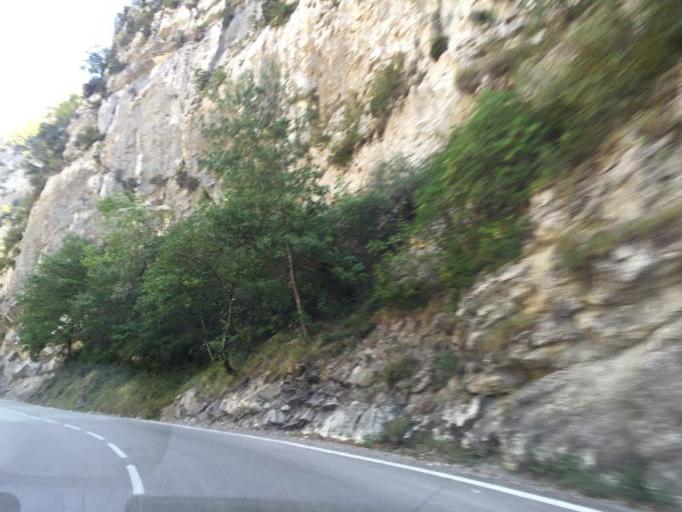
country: FR
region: Provence-Alpes-Cote d'Azur
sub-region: Departement des Alpes-Maritimes
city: Gilette
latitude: 43.9378
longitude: 7.1654
